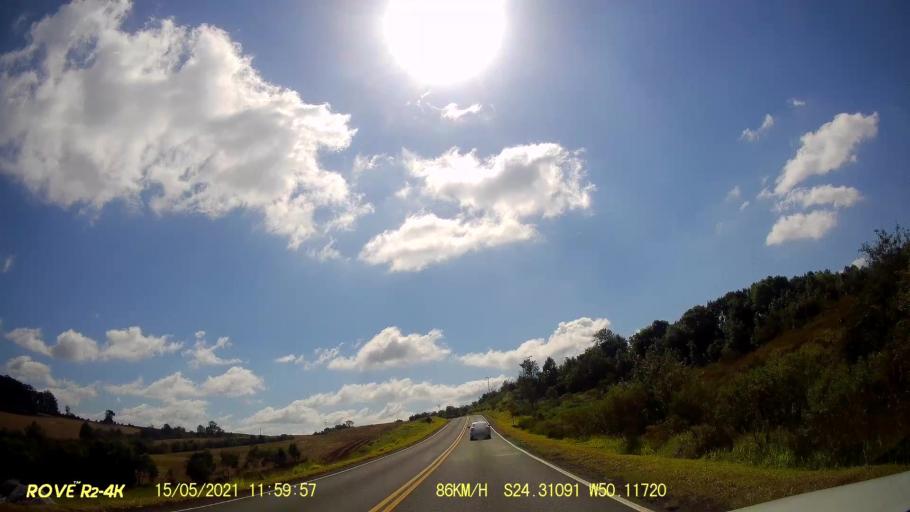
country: BR
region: Parana
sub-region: Pirai Do Sul
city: Pirai do Sul
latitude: -24.3110
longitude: -50.1172
